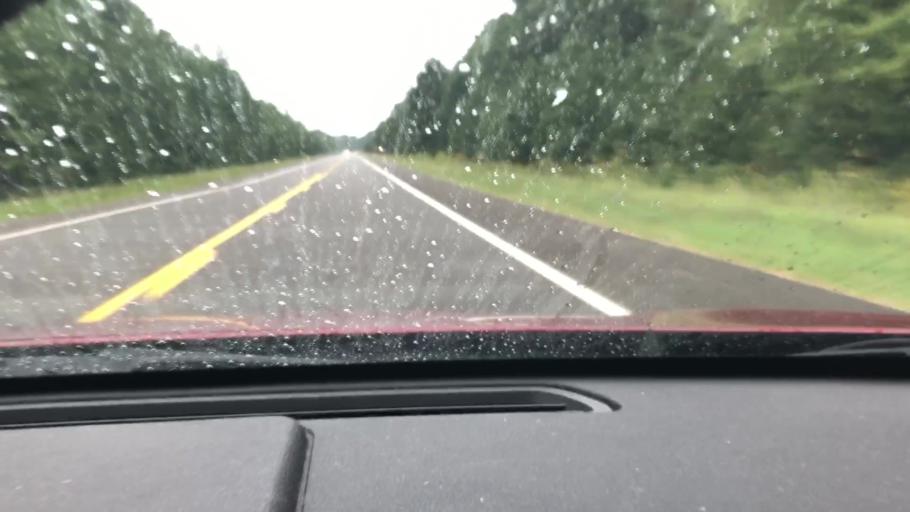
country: US
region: Arkansas
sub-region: Columbia County
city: Waldo
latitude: 33.3060
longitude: -93.2744
